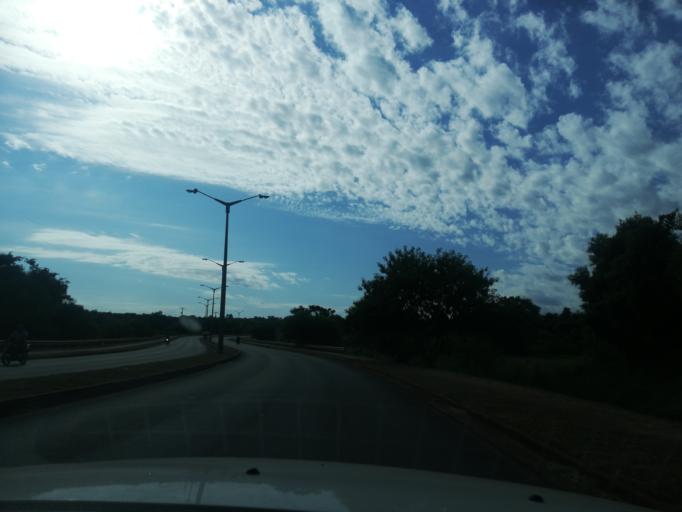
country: PY
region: Itapua
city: Encarnacion
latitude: -27.3466
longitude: -55.8518
